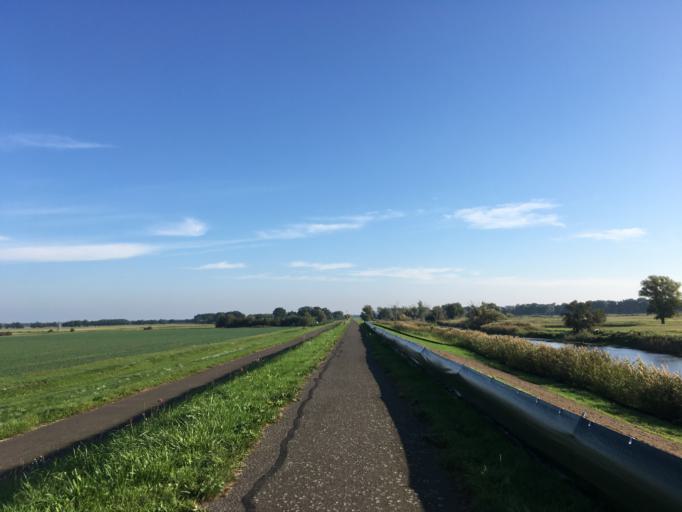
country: DE
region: Brandenburg
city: Reitwein
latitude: 52.4640
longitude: 14.5993
